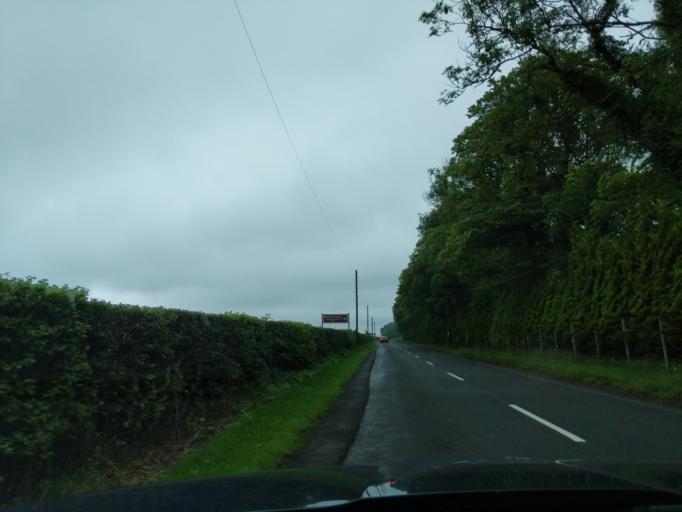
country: GB
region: England
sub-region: Northumberland
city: Lowick
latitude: 55.6488
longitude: -2.0103
